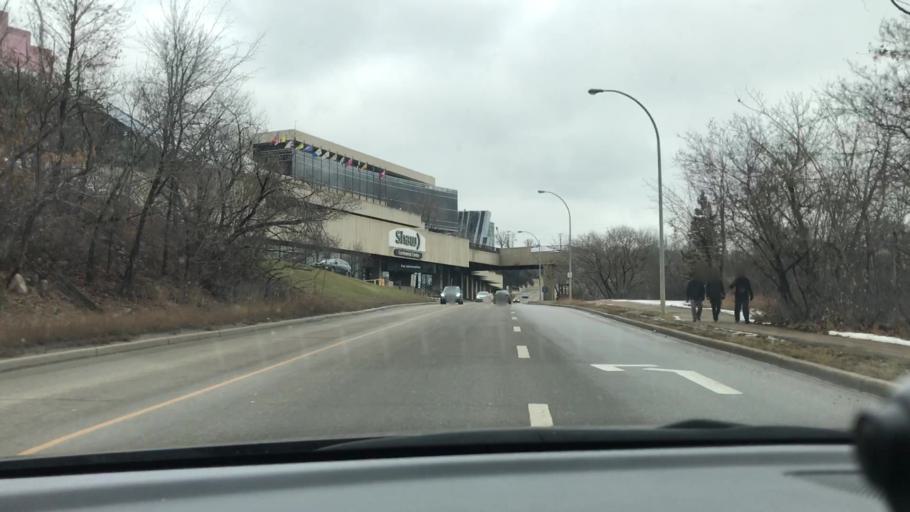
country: CA
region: Alberta
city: Edmonton
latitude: 53.5401
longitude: -113.4867
